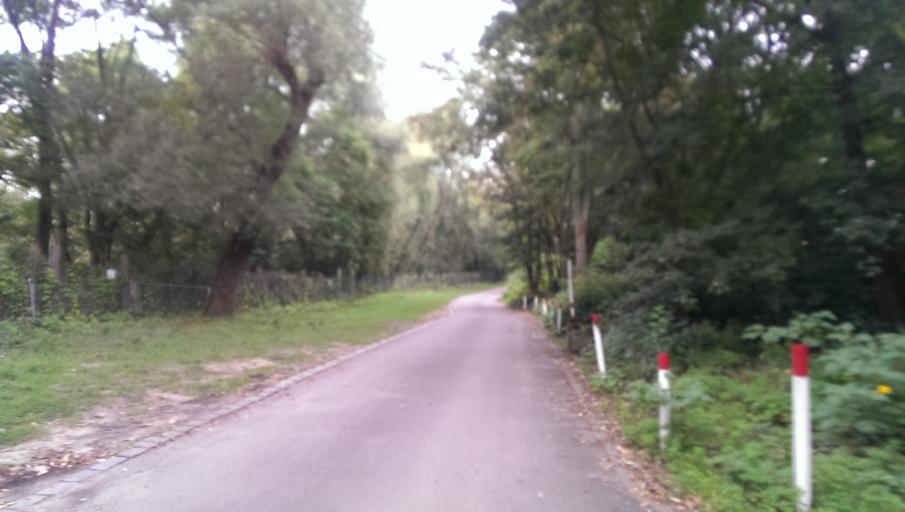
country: DE
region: Brandenburg
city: Teltow
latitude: 52.4119
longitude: 13.2832
